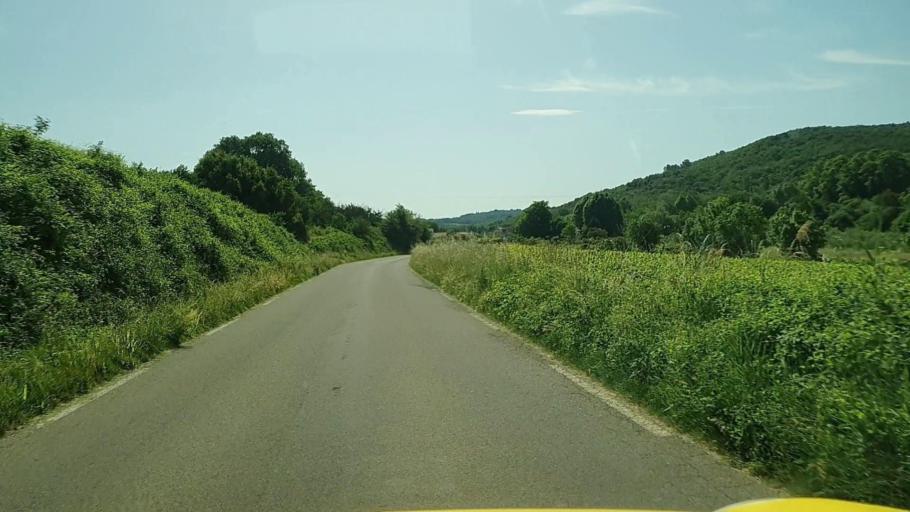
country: FR
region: Languedoc-Roussillon
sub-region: Departement du Gard
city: Tresques
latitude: 44.0973
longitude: 4.5509
